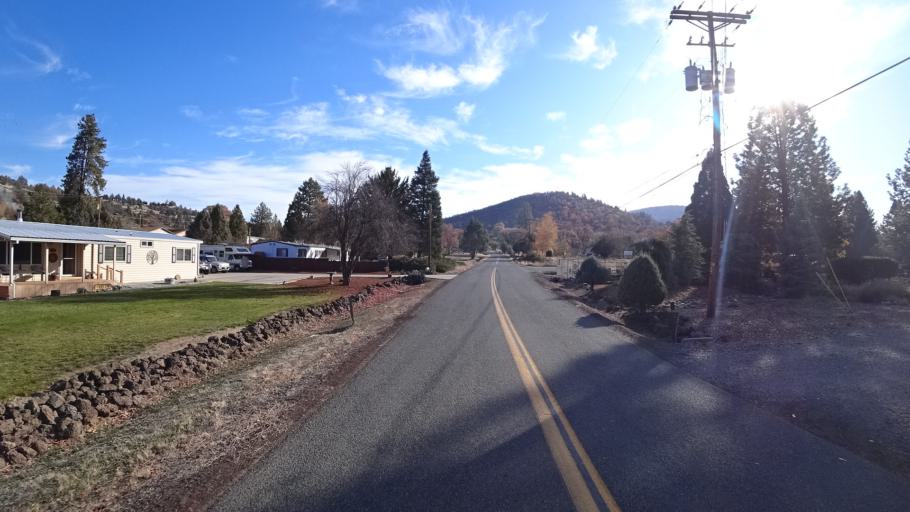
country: US
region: California
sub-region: Siskiyou County
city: Yreka
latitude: 41.6979
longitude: -122.6380
